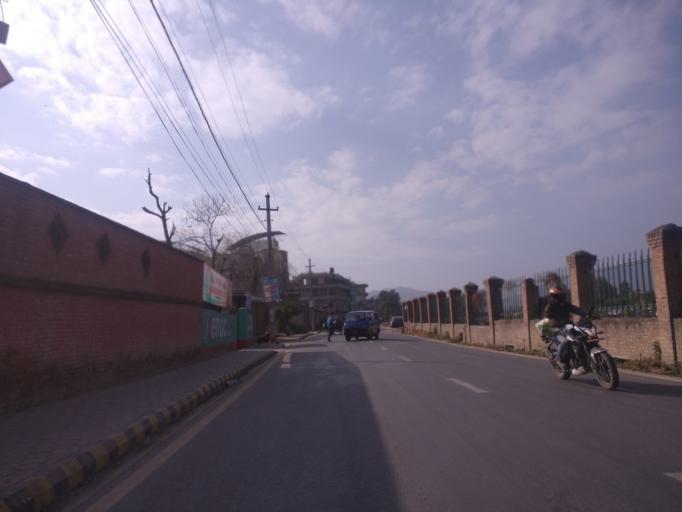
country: NP
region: Central Region
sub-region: Bagmati Zone
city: Patan
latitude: 27.6864
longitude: 85.3223
